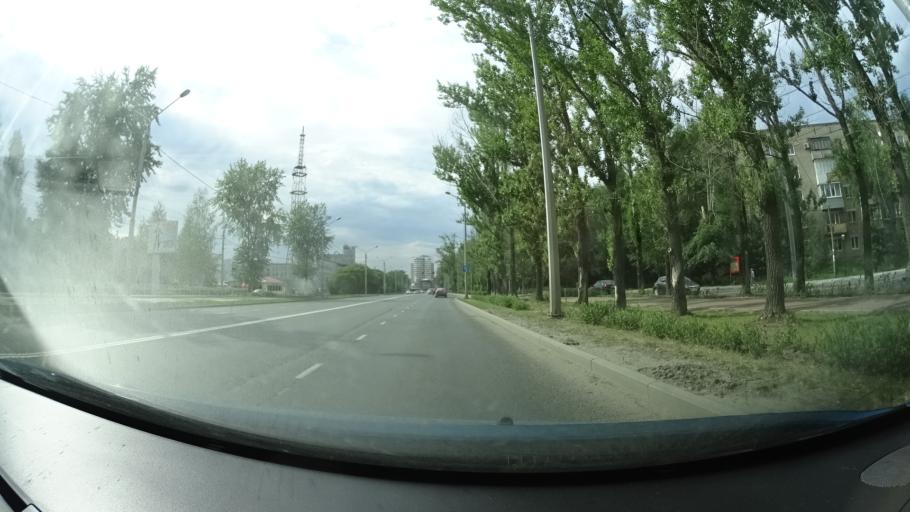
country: RU
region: Perm
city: Perm
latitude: 57.9915
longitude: 56.2943
